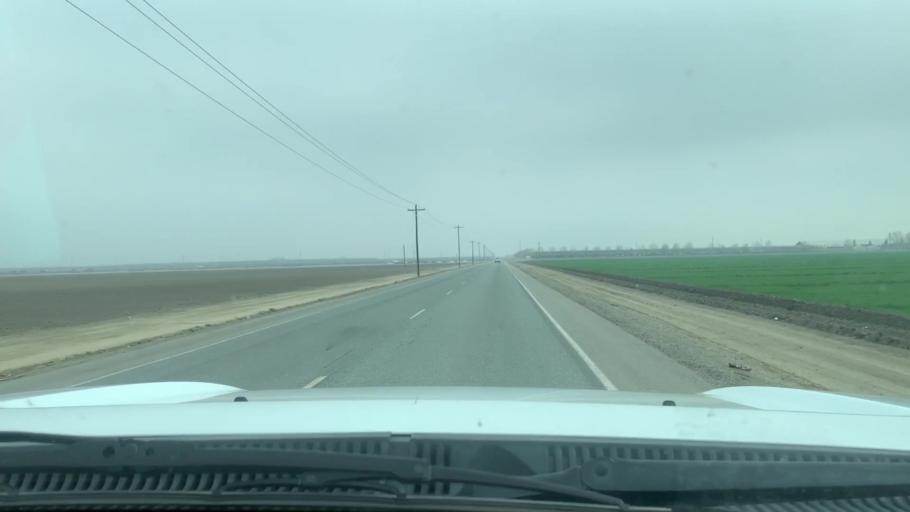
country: US
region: California
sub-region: Kern County
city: Buttonwillow
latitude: 35.5005
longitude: -119.4630
